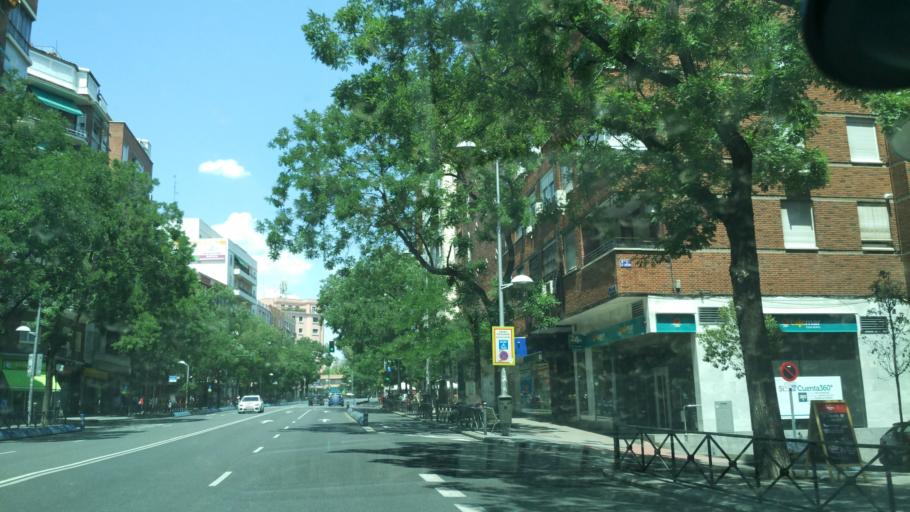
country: ES
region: Madrid
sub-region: Provincia de Madrid
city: Tetuan de las Victorias
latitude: 40.4554
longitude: -3.7025
